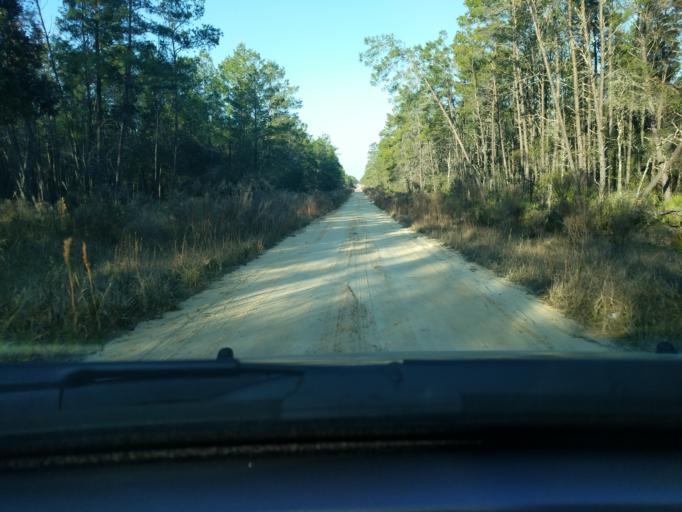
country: US
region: Florida
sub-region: Lake County
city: Astor
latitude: 29.2260
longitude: -81.7637
